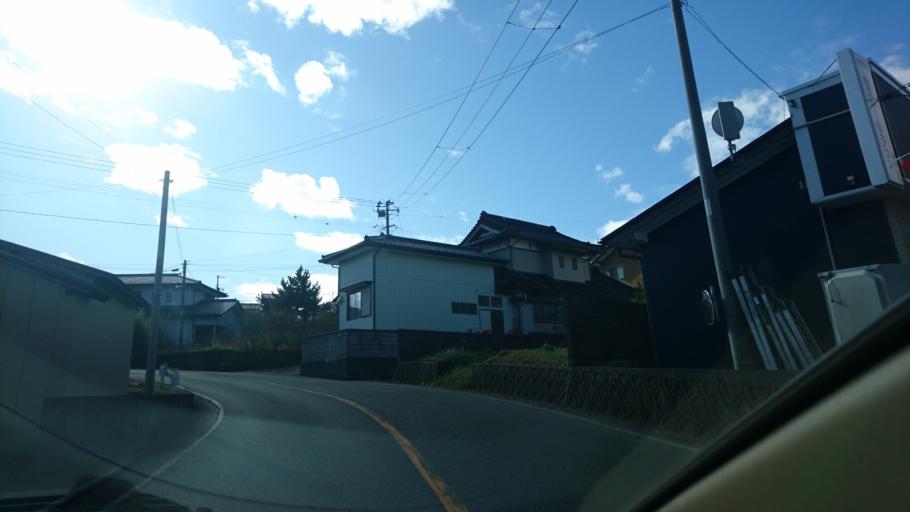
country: JP
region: Iwate
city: Ofunato
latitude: 39.0123
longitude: 141.7137
